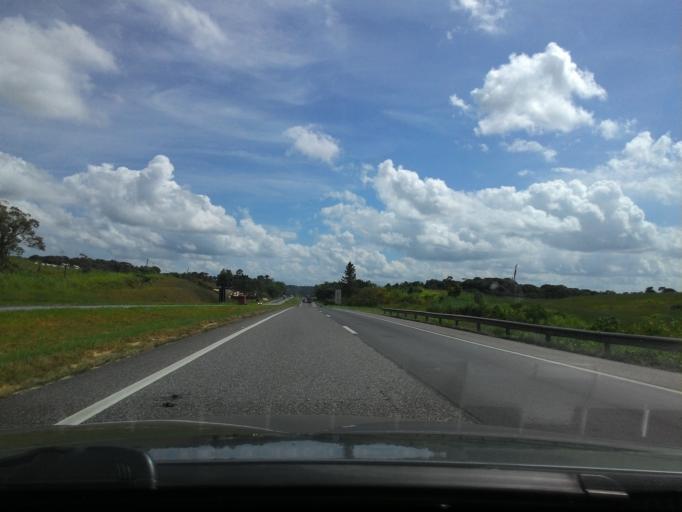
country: BR
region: Sao Paulo
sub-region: Pariquera-Acu
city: Pariquera Acu
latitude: -24.6348
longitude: -47.9087
